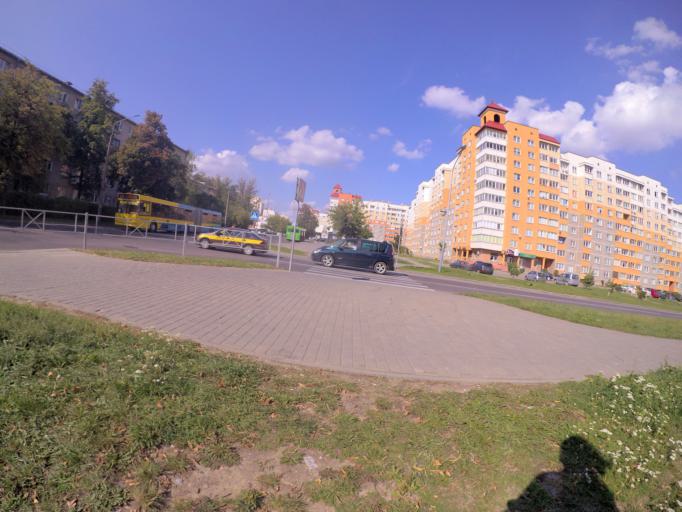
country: BY
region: Grodnenskaya
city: Hrodna
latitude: 53.6944
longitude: 23.8352
